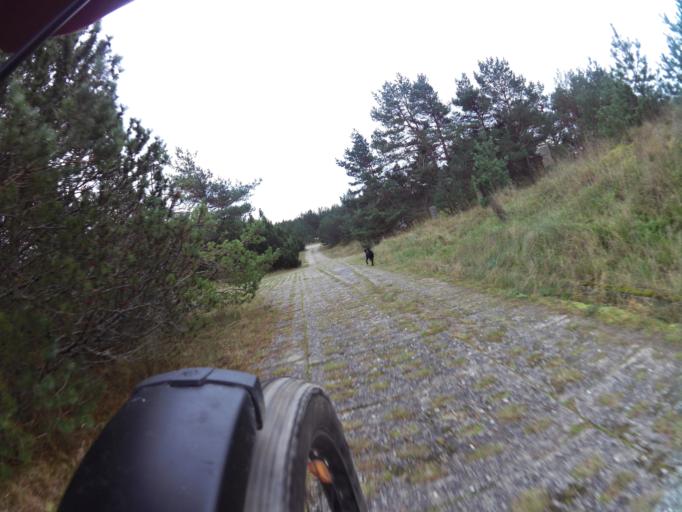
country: PL
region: Pomeranian Voivodeship
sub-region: Powiat leborski
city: Leba
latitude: 54.7693
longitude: 17.5937
